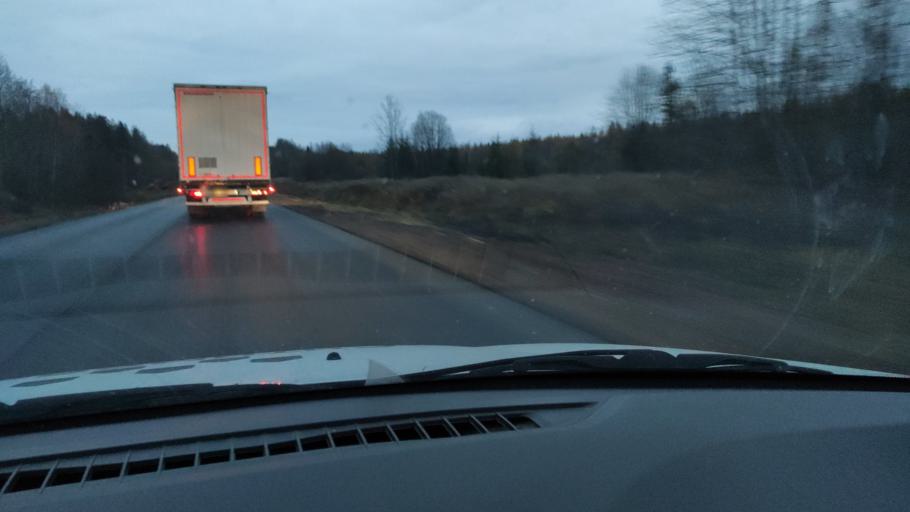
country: RU
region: Kirov
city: Kostino
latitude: 58.8193
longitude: 53.3460
